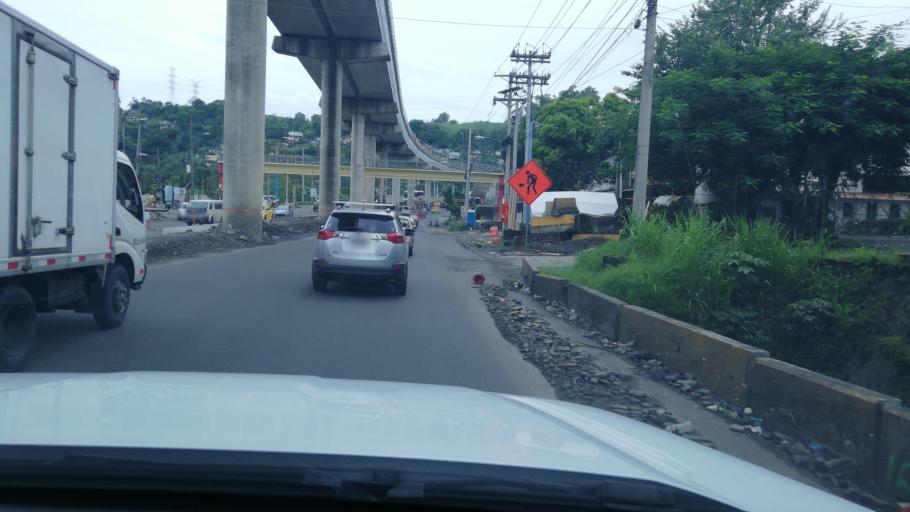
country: PA
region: Panama
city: Las Cumbres
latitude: 9.0642
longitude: -79.5126
